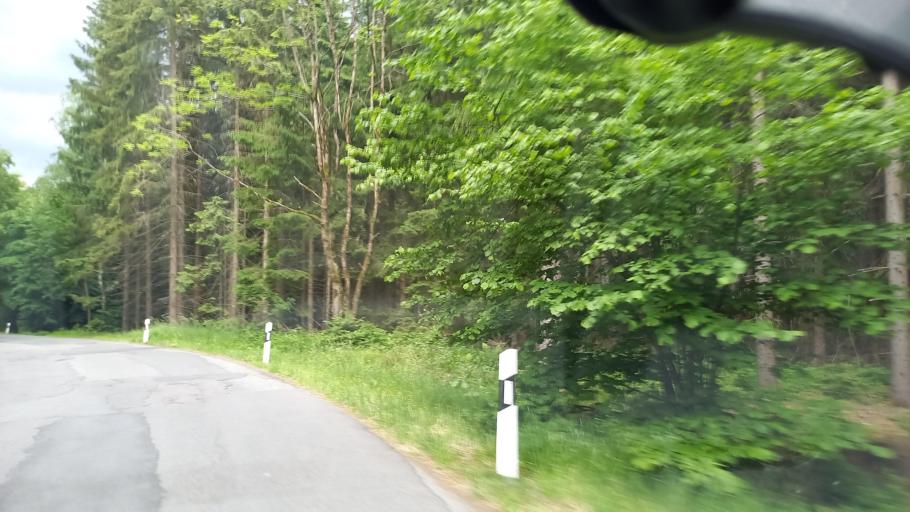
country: DE
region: Saxony
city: Rodewisch
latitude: 50.5484
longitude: 12.4677
